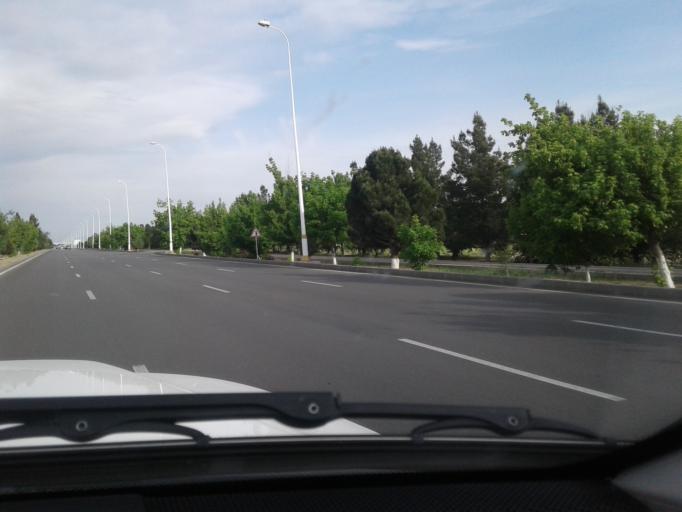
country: TM
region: Ahal
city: Ashgabat
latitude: 38.0043
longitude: 58.2921
